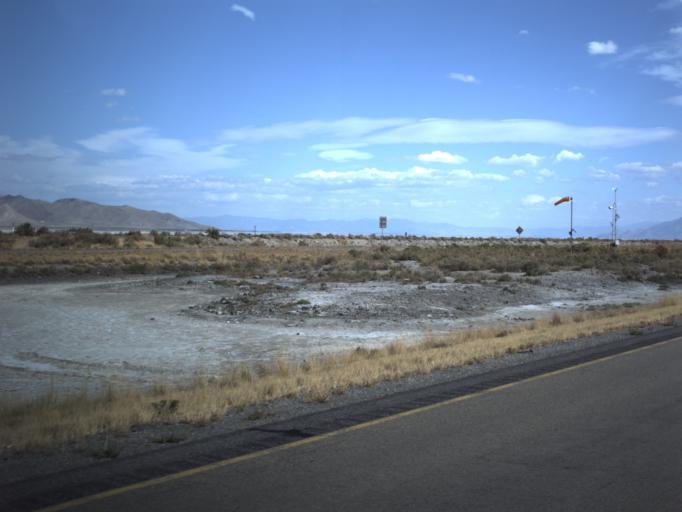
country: US
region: Utah
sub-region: Tooele County
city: Grantsville
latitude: 40.7403
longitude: -112.6247
